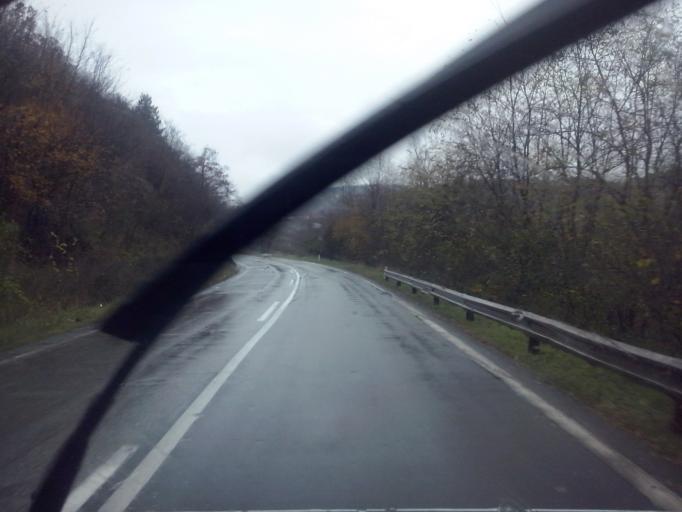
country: RS
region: Central Serbia
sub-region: Raski Okrug
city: Raska
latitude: 43.3586
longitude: 20.6443
